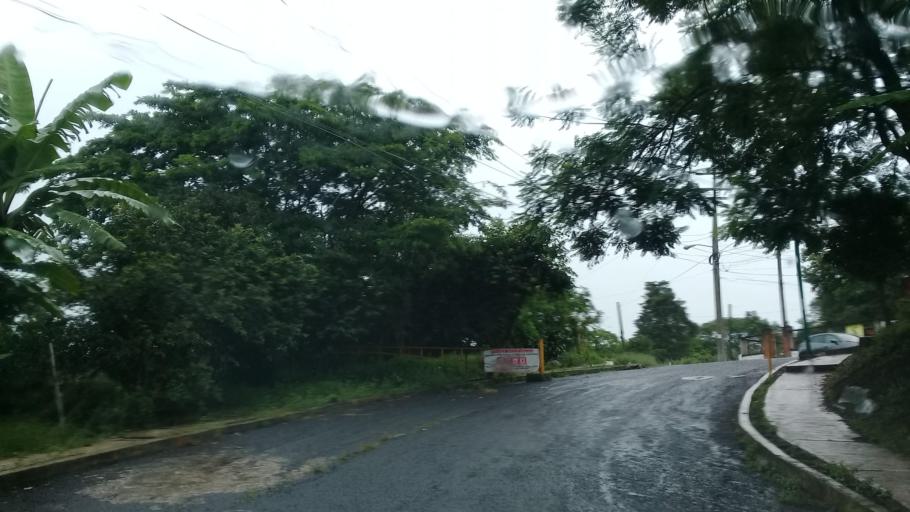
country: MX
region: Veracruz
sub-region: Xalapa
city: Lomas Verdes
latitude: 19.5145
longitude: -96.9000
